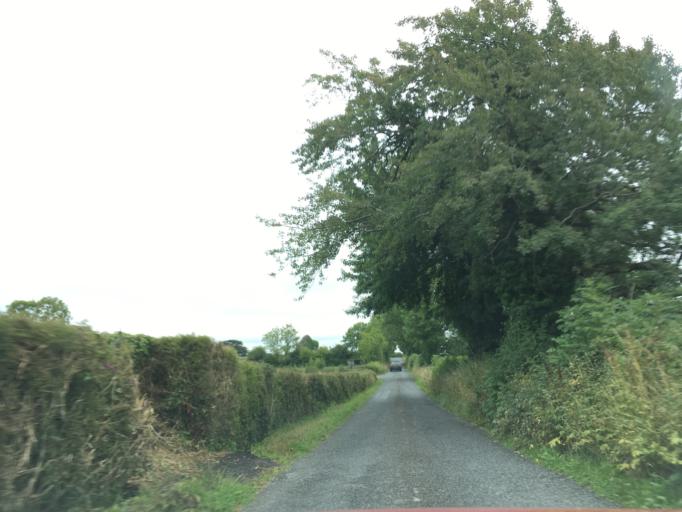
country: IE
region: Munster
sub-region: An Clar
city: Ennis
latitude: 52.7192
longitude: -9.0825
